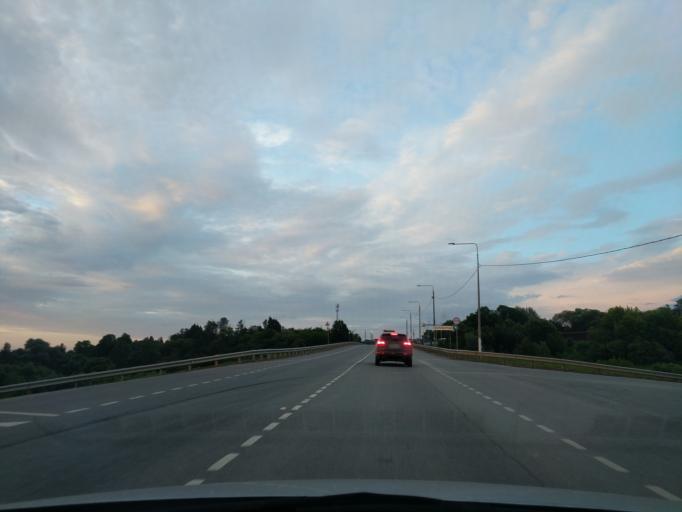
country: RU
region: Kaluga
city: Maloyaroslavets
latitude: 55.0272
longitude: 36.5165
